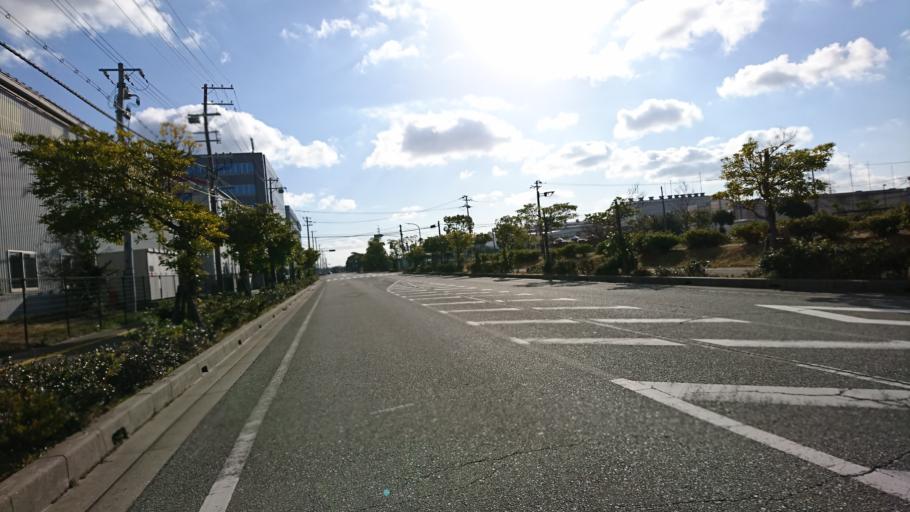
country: JP
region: Hyogo
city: Kakogawacho-honmachi
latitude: 34.7562
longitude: 134.7883
